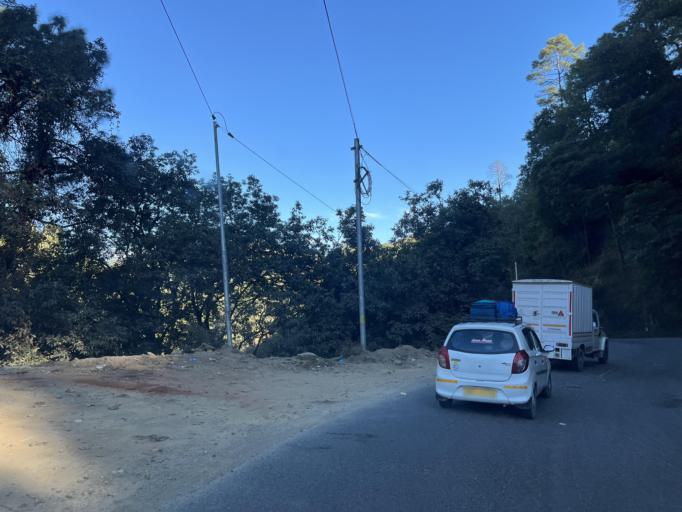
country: IN
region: Uttarakhand
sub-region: Naini Tal
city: Bhowali
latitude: 29.3945
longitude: 79.5112
